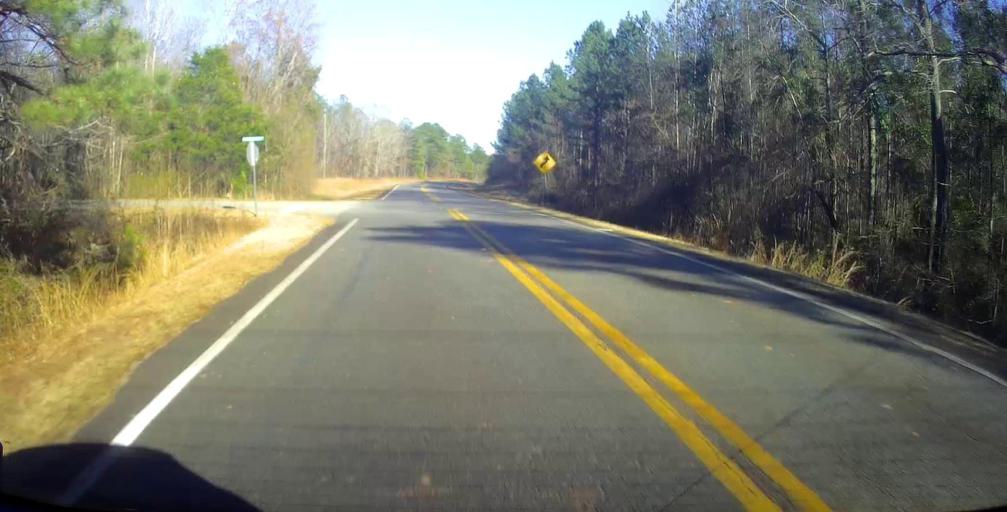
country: US
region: Georgia
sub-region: Talbot County
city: Sardis
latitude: 32.7780
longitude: -84.6737
